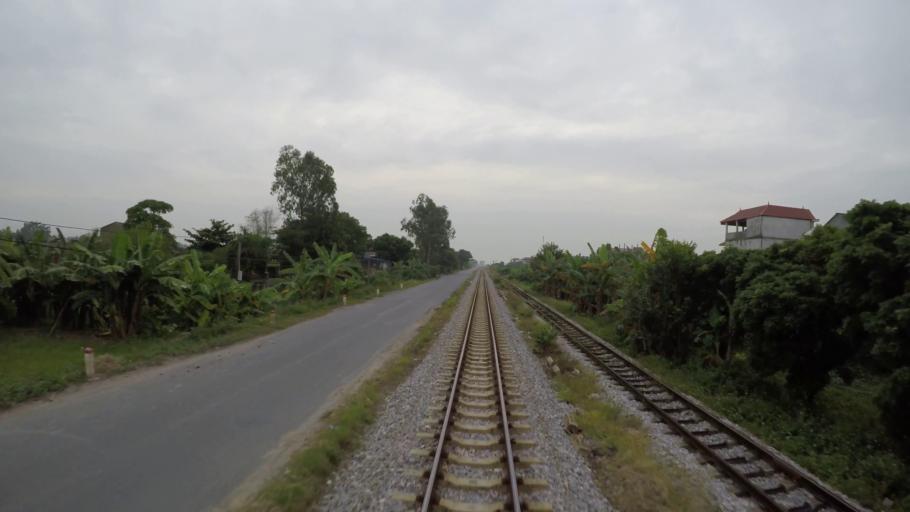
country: VN
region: Hung Yen
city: Ban Yen Nhan
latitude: 20.9733
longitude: 106.0950
